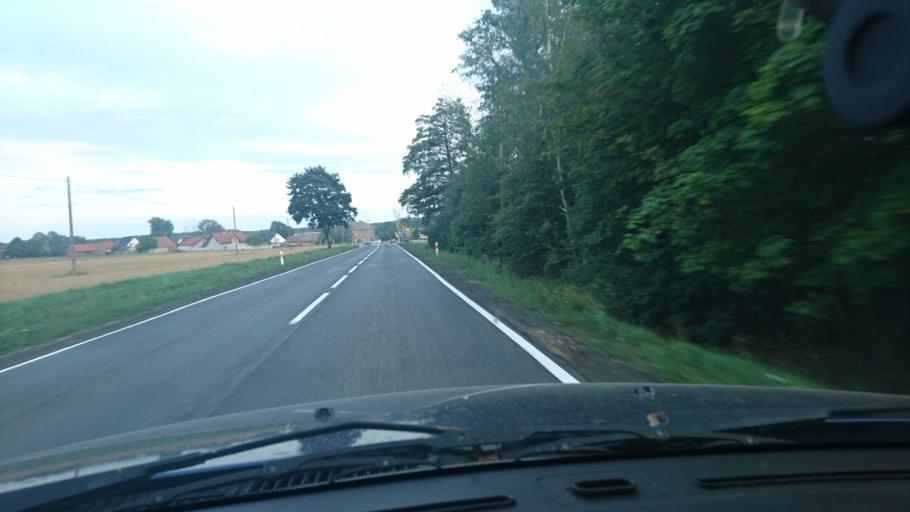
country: PL
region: Silesian Voivodeship
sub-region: Powiat lubliniecki
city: Sierakow Slaski
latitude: 50.8279
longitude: 18.5265
